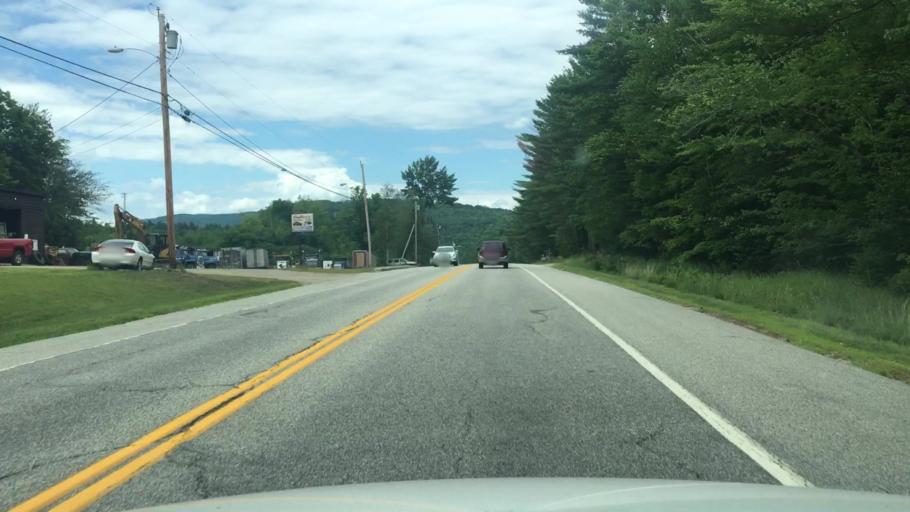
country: US
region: Maine
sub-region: Oxford County
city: West Paris
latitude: 44.3457
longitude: -70.5625
